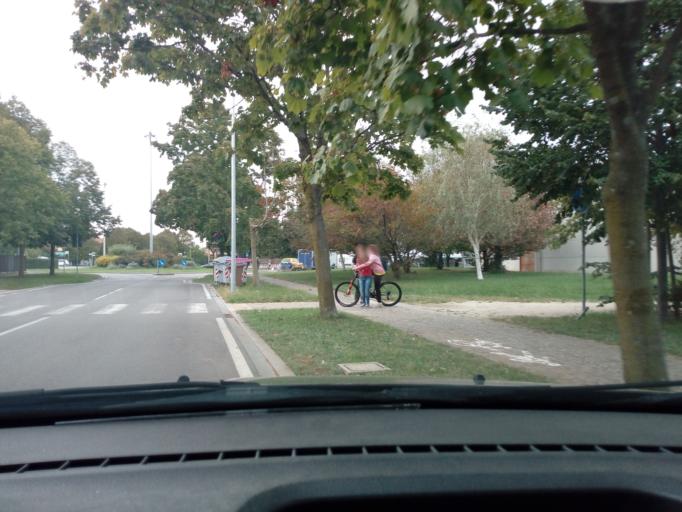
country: IT
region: Friuli Venezia Giulia
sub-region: Provincia di Udine
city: Cividale del Friuli
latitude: 46.0854
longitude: 13.4324
